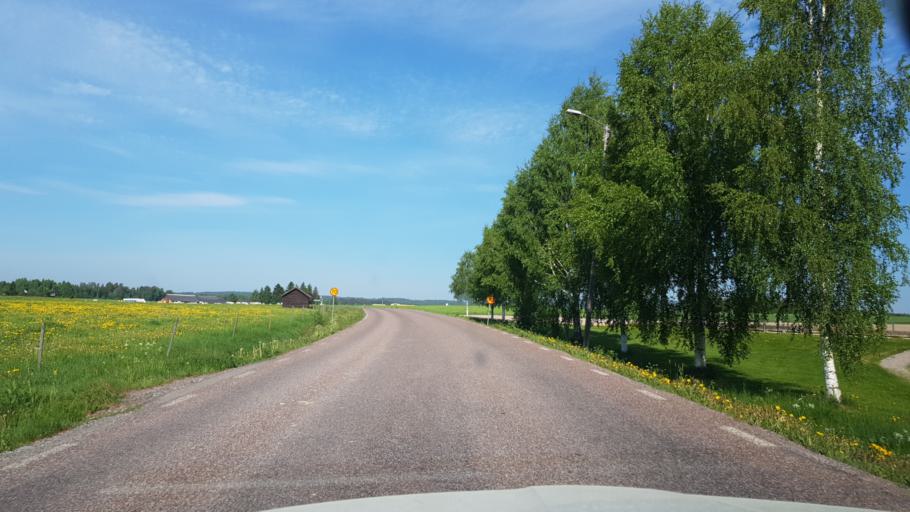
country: SE
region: Dalarna
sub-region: Saters Kommun
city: Saeter
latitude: 60.4161
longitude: 15.7627
